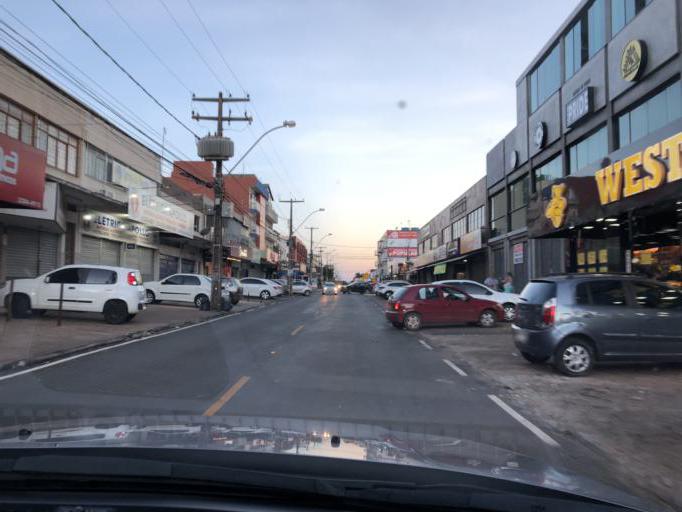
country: BR
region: Federal District
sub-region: Brasilia
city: Brasilia
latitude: -15.8112
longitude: -48.0630
